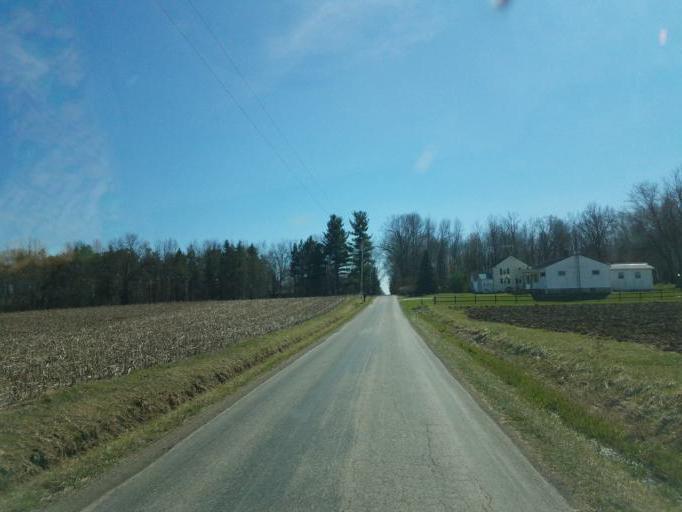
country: US
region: Ohio
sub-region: Ashland County
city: Ashland
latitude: 40.8893
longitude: -82.3682
